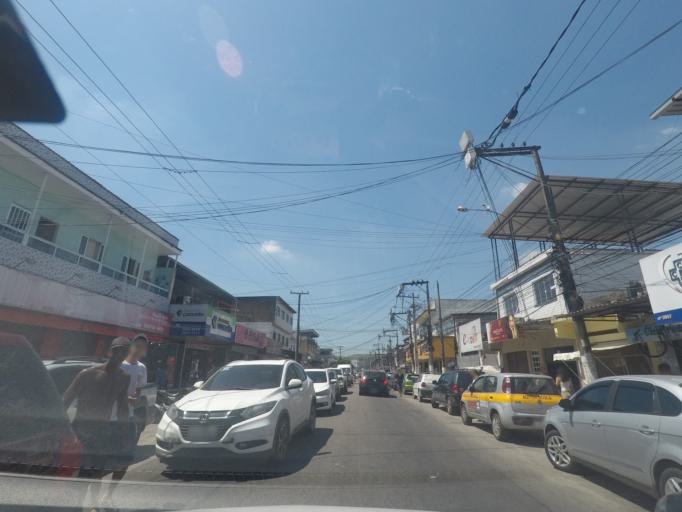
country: BR
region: Rio de Janeiro
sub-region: Petropolis
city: Petropolis
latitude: -22.5901
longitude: -43.1864
